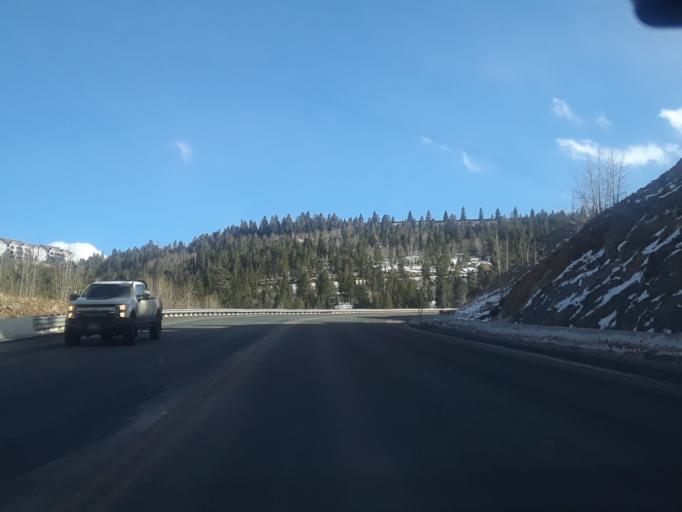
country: US
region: Colorado
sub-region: Gilpin County
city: Central City
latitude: 39.7948
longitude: -105.5156
